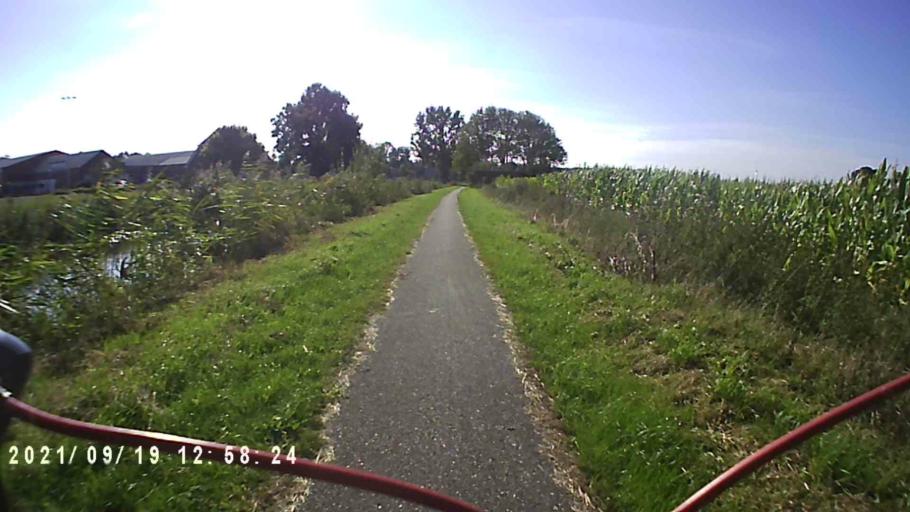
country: NL
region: Groningen
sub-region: Gemeente  Oldambt
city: Winschoten
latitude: 53.1868
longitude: 6.9511
